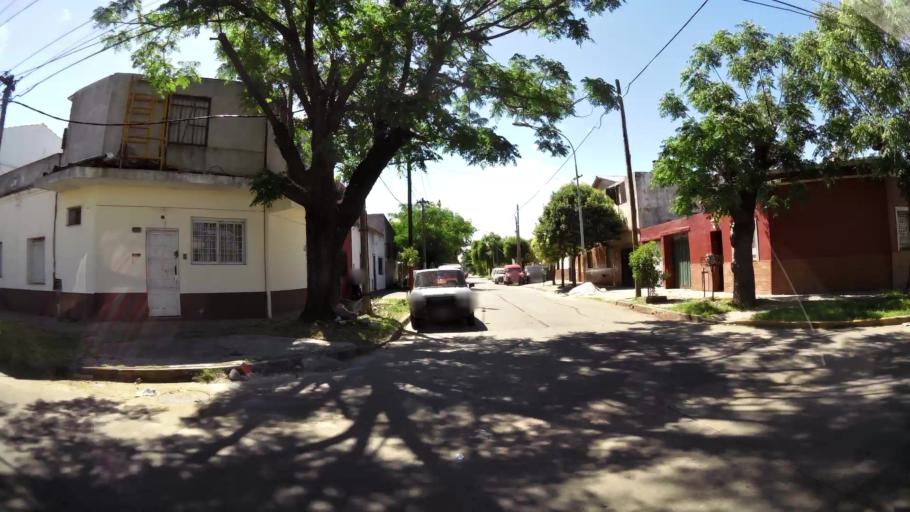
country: AR
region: Buenos Aires
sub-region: Partido de General San Martin
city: General San Martin
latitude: -34.5293
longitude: -58.5596
